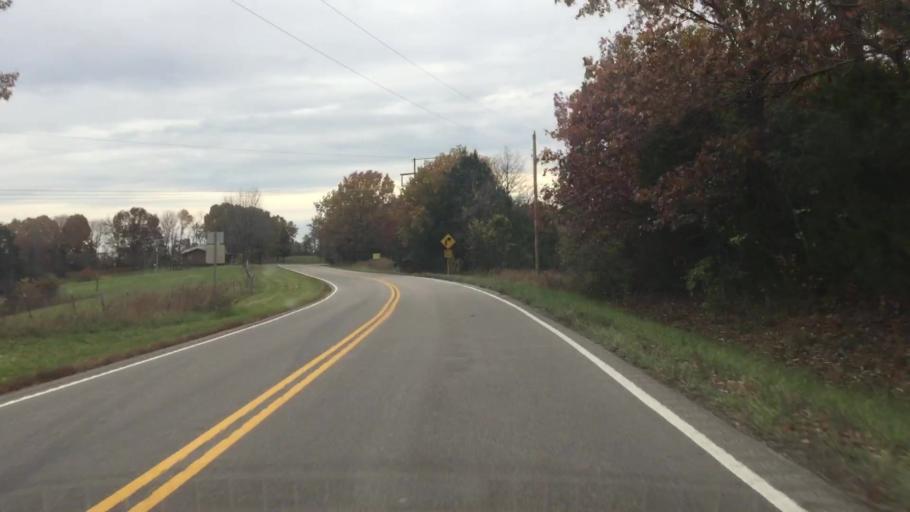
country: US
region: Missouri
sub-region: Gasconade County
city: Hermann
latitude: 38.7223
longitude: -91.7063
